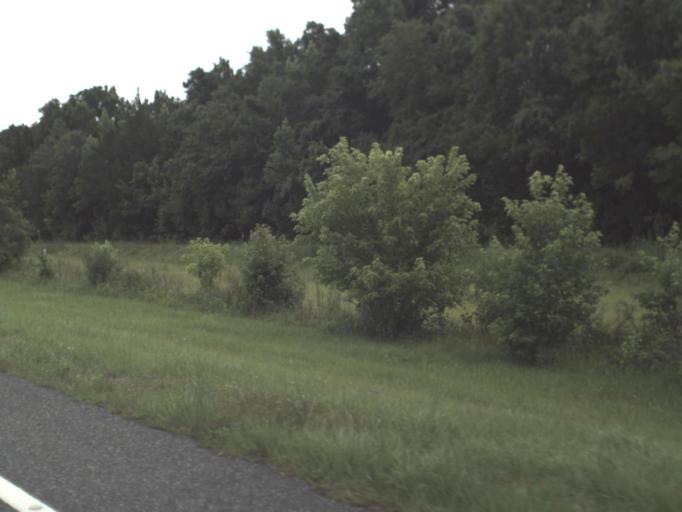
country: US
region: Florida
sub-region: Levy County
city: Williston Highlands
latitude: 29.2435
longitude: -82.7172
